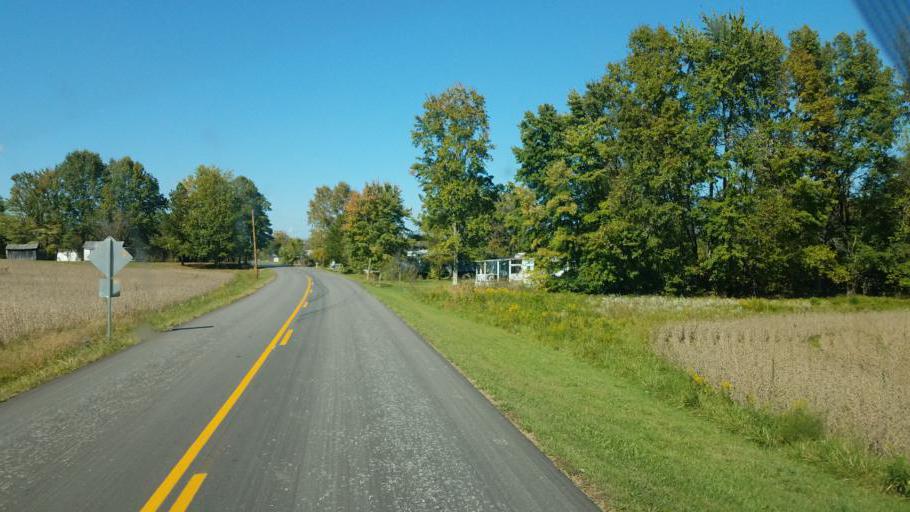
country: US
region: Kentucky
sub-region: Fleming County
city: Flemingsburg
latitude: 38.4649
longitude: -83.5872
